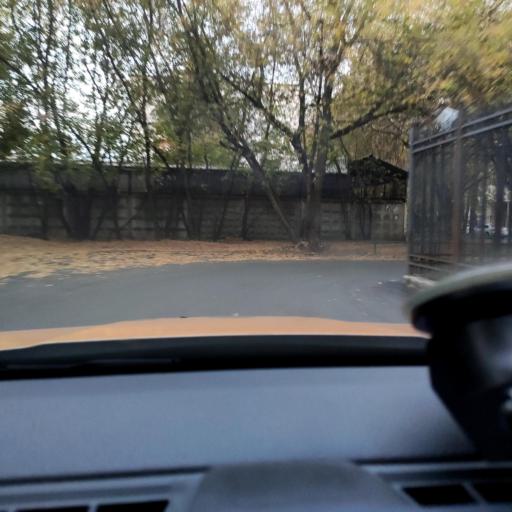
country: RU
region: Moscow
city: Yaroslavskiy
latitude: 55.8639
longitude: 37.7029
